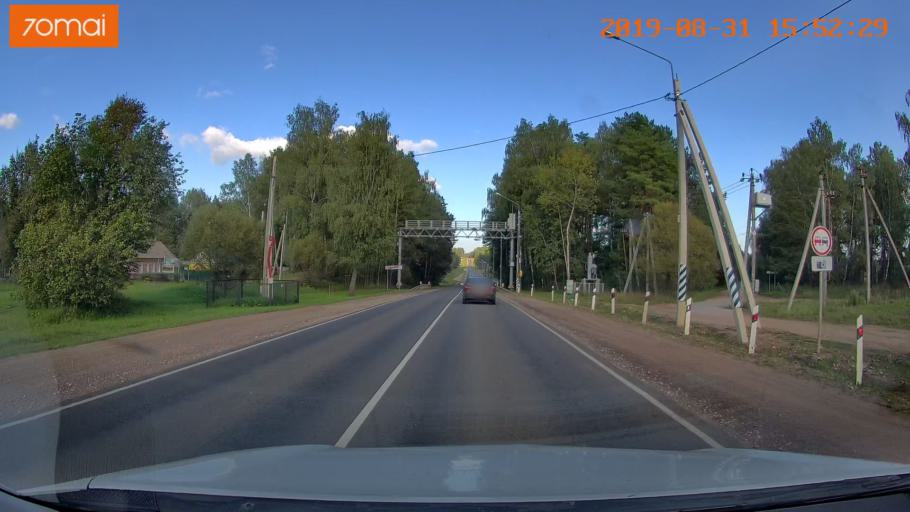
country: RU
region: Kaluga
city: Yukhnov
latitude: 54.7083
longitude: 35.1144
